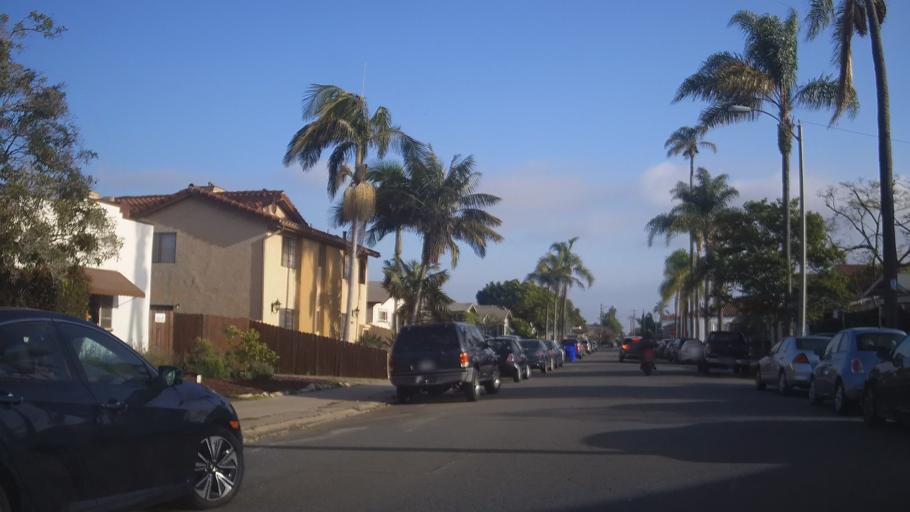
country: US
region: California
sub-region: San Diego County
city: San Diego
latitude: 32.7451
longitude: -117.1292
